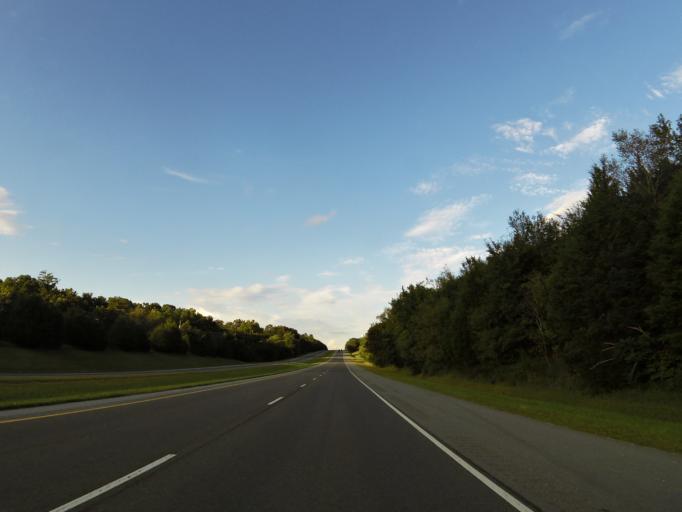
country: US
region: Tennessee
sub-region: Knox County
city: Mascot
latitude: 36.0568
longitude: -83.7915
